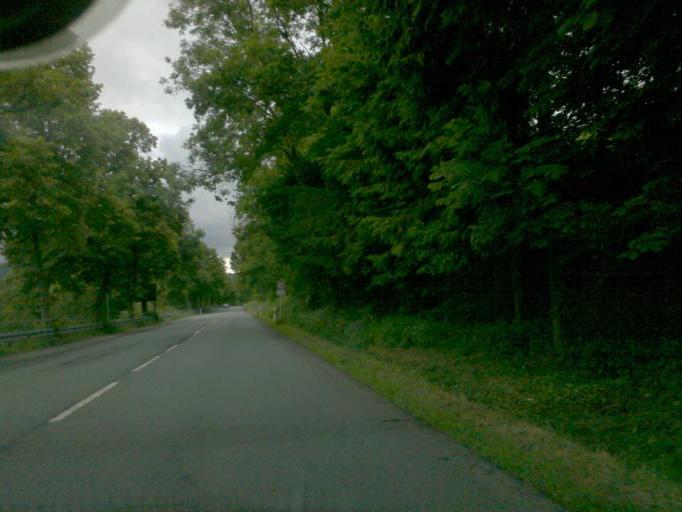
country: DE
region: North Rhine-Westphalia
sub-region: Regierungsbezirk Arnsberg
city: Meschede
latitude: 51.2996
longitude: 8.2587
